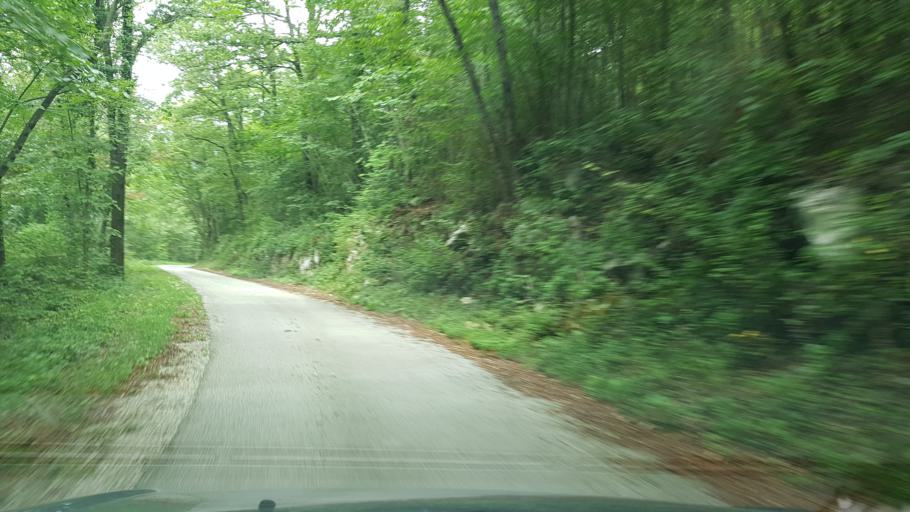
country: SI
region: Kanal
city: Deskle
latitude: 46.0253
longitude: 13.6111
